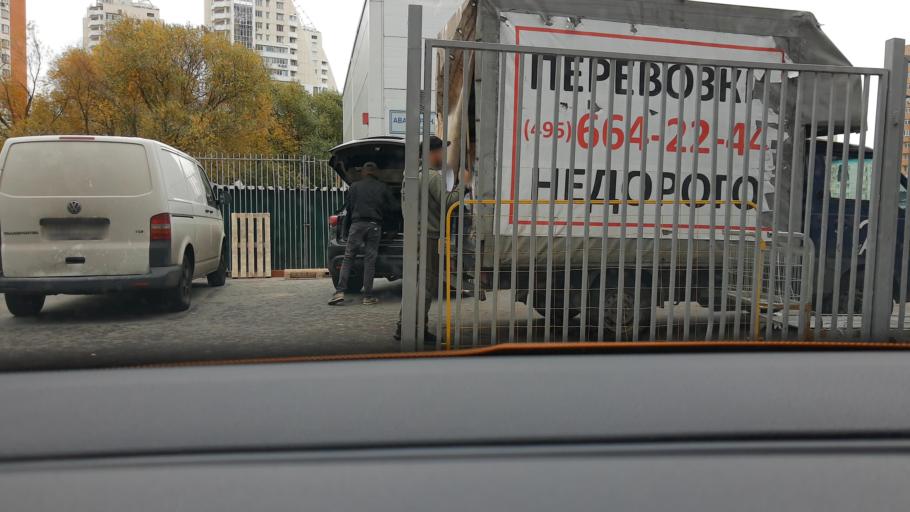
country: RU
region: Moskovskaya
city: Pavshino
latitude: 55.8136
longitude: 37.3634
